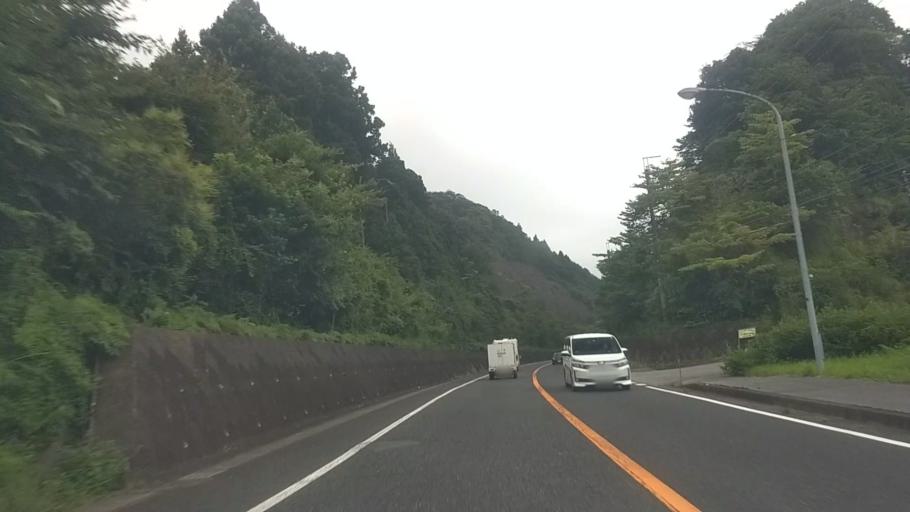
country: JP
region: Chiba
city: Kawaguchi
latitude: 35.1825
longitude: 140.0615
